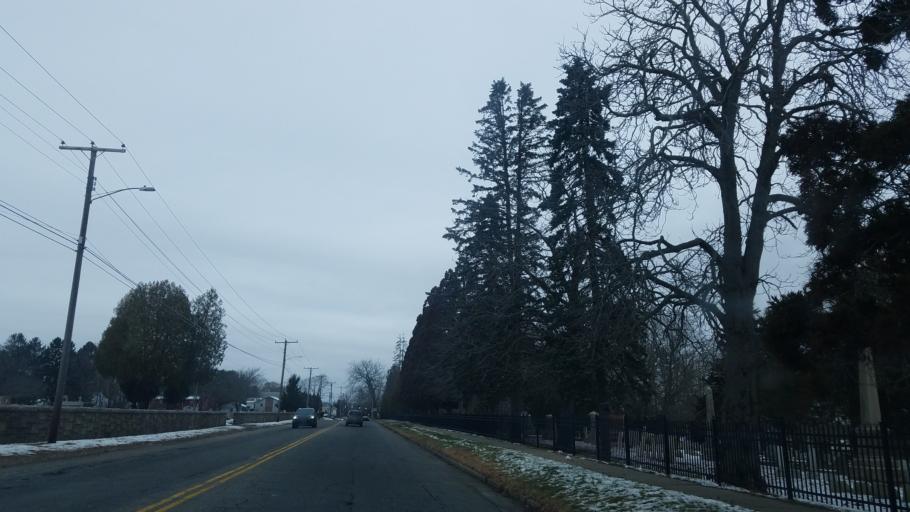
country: US
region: Connecticut
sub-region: New London County
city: Central Waterford
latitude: 41.3650
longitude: -72.1255
